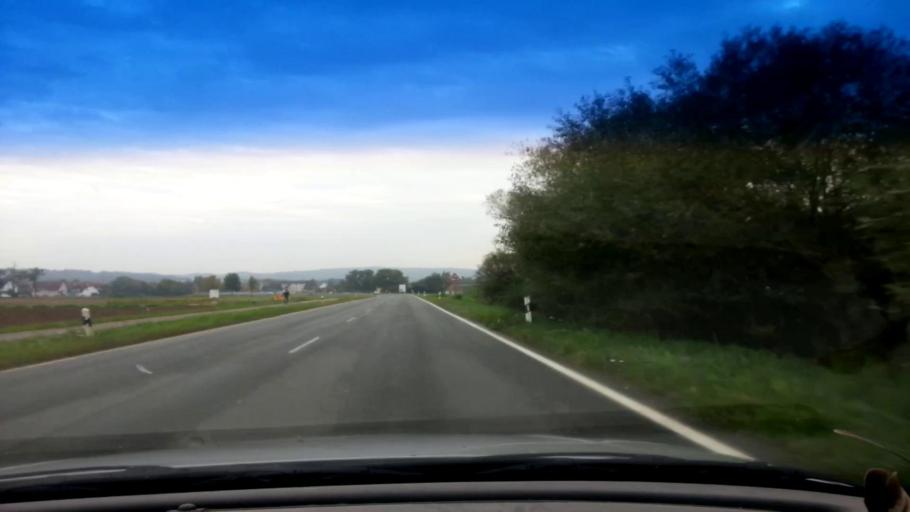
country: DE
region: Bavaria
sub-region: Upper Franconia
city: Zapfendorf
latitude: 50.0272
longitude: 10.9387
